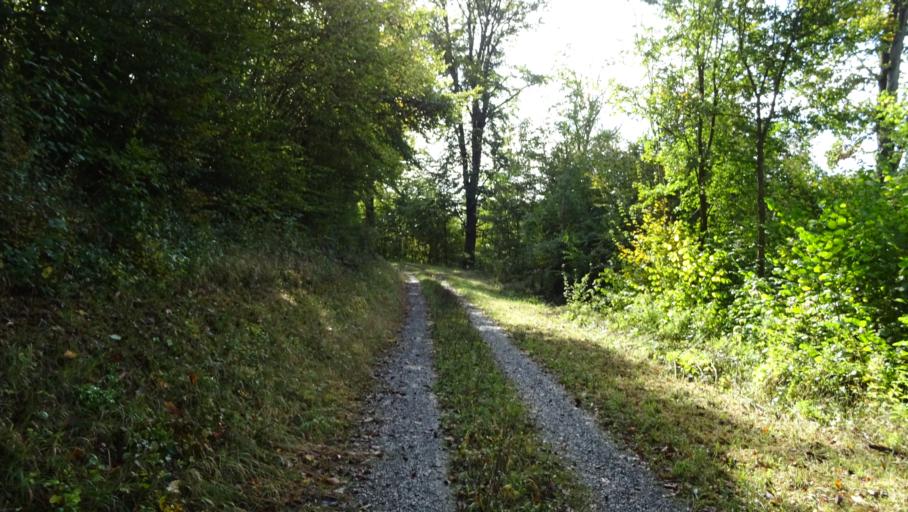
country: DE
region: Baden-Wuerttemberg
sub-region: Karlsruhe Region
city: Billigheim
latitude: 49.3667
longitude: 9.2657
